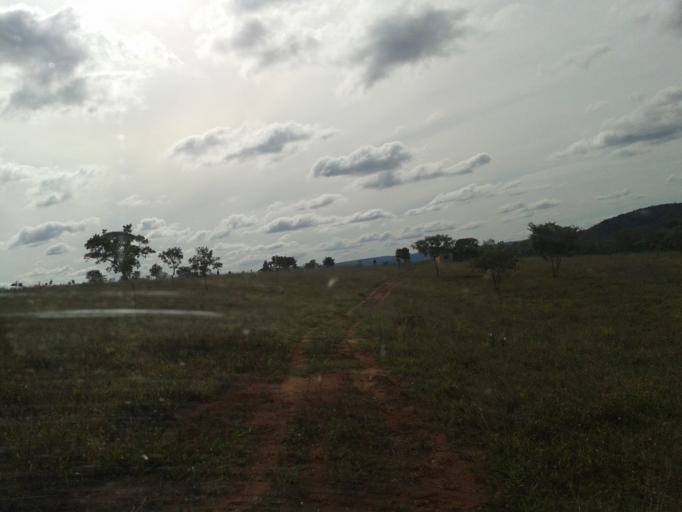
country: BR
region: Minas Gerais
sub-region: Campina Verde
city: Campina Verde
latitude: -19.4347
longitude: -49.7236
